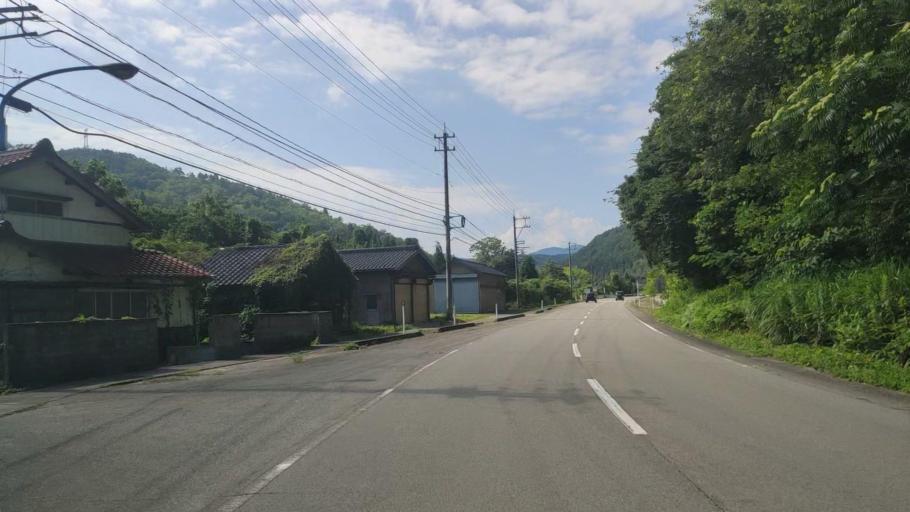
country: JP
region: Ishikawa
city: Komatsu
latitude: 36.3553
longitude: 136.5047
